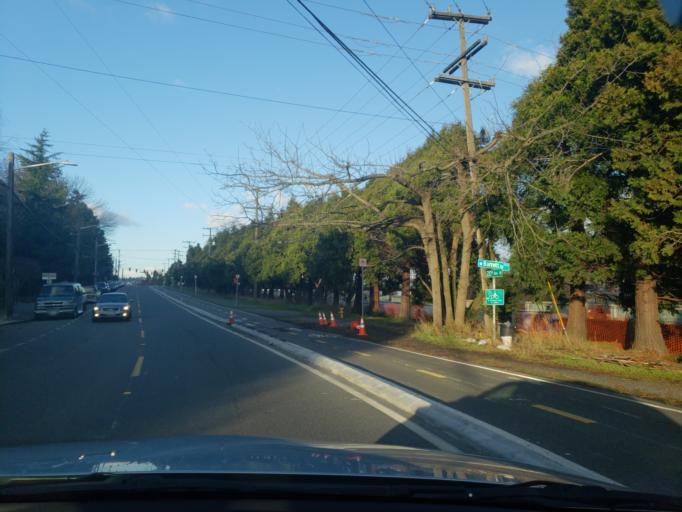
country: US
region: Washington
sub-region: King County
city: Seattle
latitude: 47.6464
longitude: -122.3821
